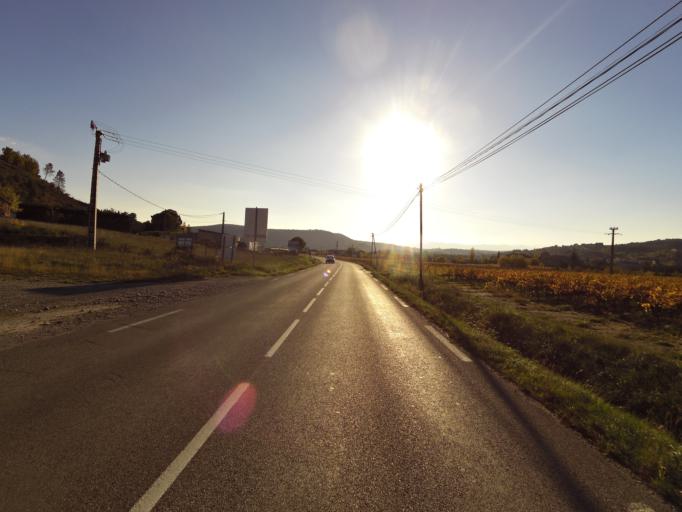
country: FR
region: Rhone-Alpes
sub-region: Departement de l'Ardeche
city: Rosieres
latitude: 44.4896
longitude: 4.2721
